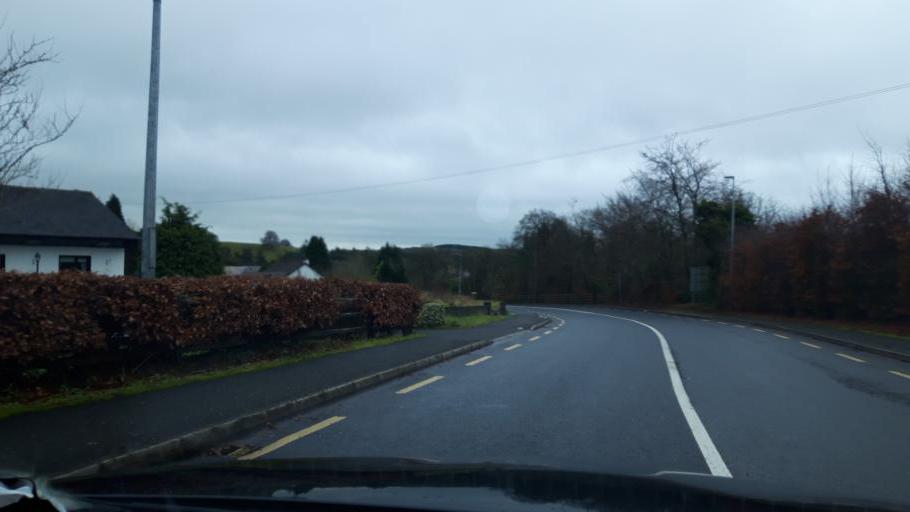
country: IE
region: Ulster
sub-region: County Monaghan
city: Castleblayney
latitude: 54.1116
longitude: -6.7325
